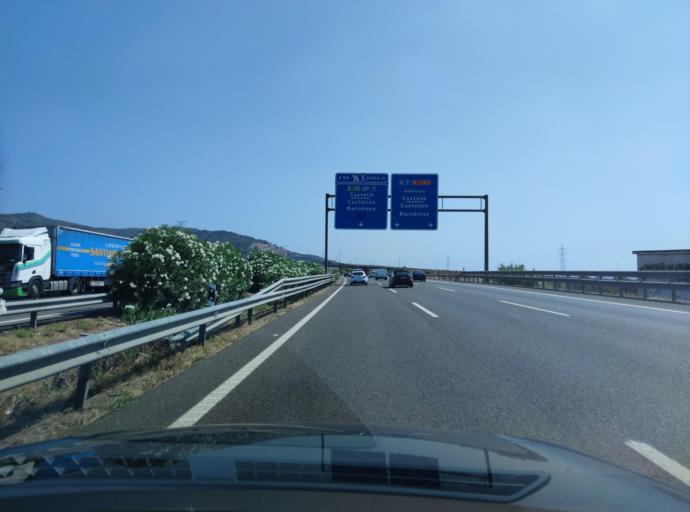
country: ES
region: Valencia
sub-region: Provincia de Valencia
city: Petres
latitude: 39.6891
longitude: -0.2876
